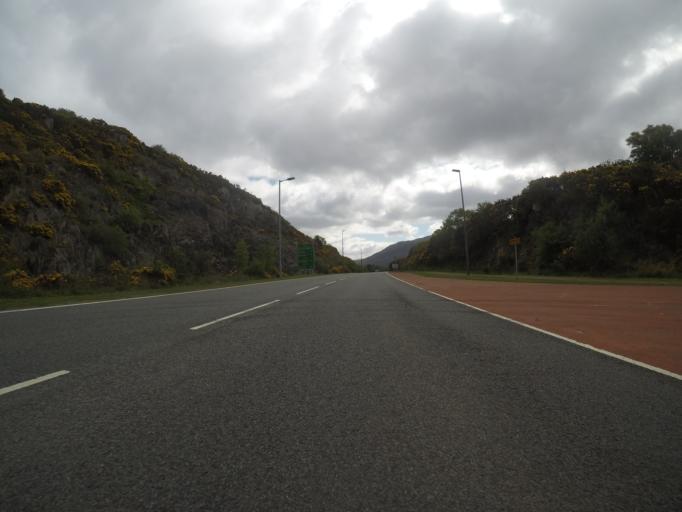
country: GB
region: Scotland
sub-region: Highland
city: Portree
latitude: 57.2814
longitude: -5.7261
